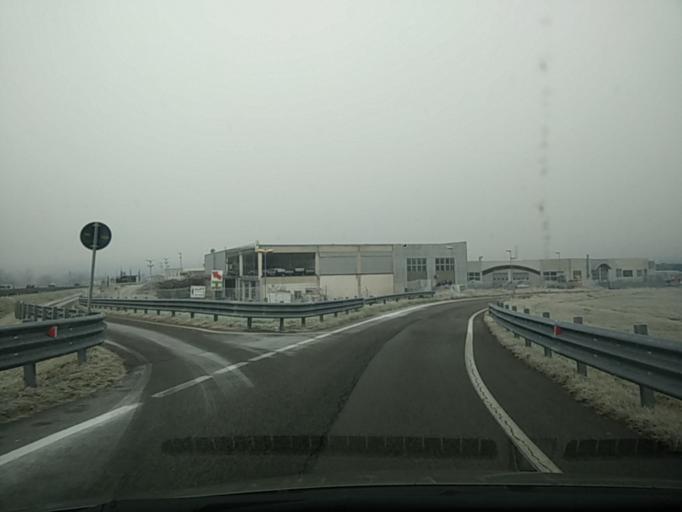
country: IT
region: Veneto
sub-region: Provincia di Belluno
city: Fonzaso
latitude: 46.0022
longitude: 11.8212
